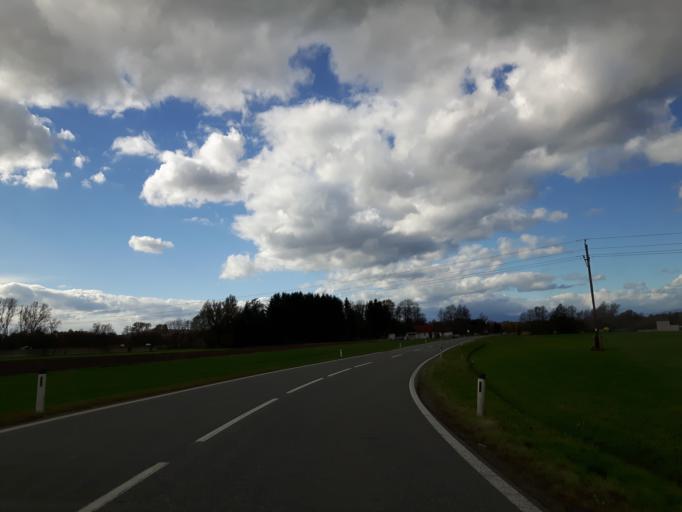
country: AT
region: Styria
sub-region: Politischer Bezirk Leibnitz
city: Ragnitz
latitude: 46.8308
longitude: 15.5939
